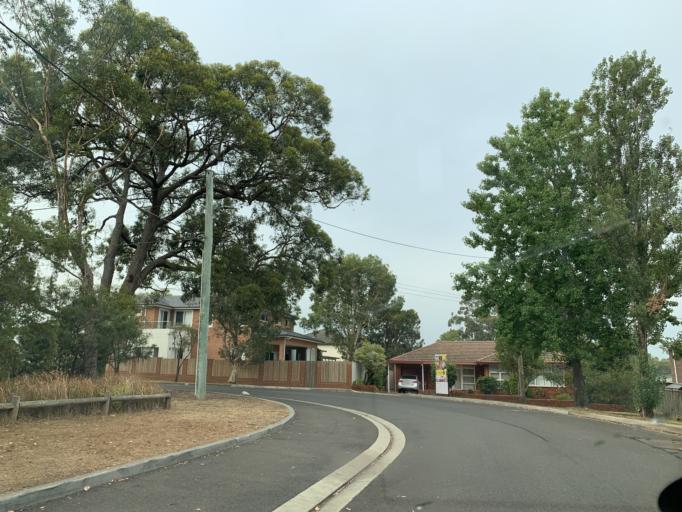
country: AU
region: New South Wales
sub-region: Parramatta
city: Dundas Valley
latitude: -33.7767
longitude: 151.0644
